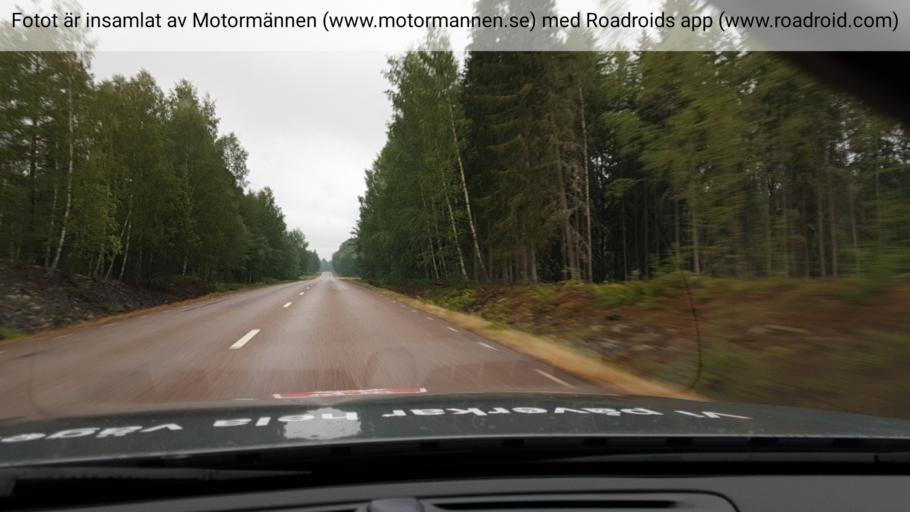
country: SE
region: Dalarna
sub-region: Avesta Kommun
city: Avesta
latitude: 59.9691
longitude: 16.1704
